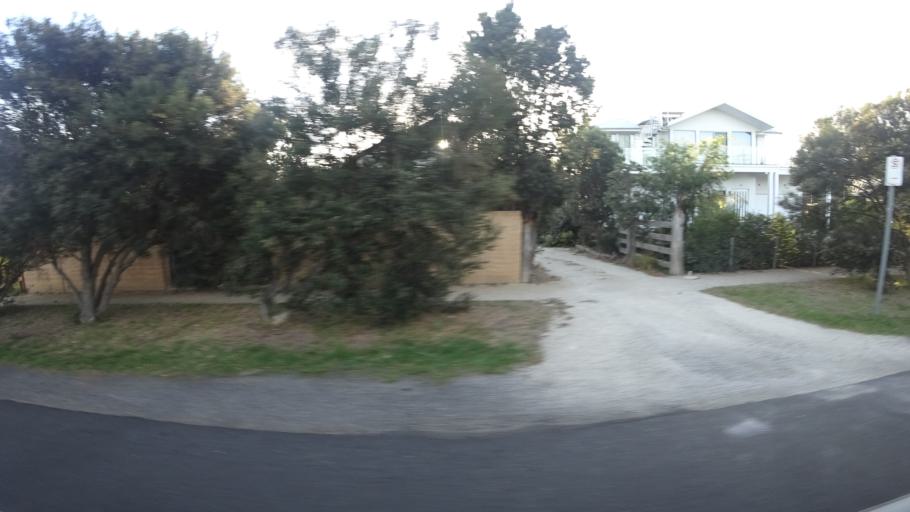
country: AU
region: Victoria
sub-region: Queenscliffe
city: Queenscliff
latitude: -38.2762
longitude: 144.6179
